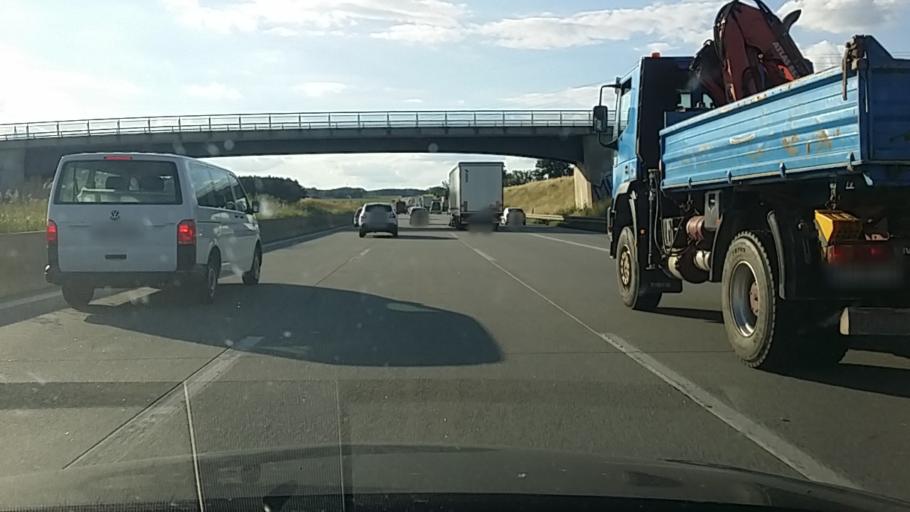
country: DE
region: Bavaria
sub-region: Upper Bavaria
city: Sulzemoos
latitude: 48.2598
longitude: 11.2989
